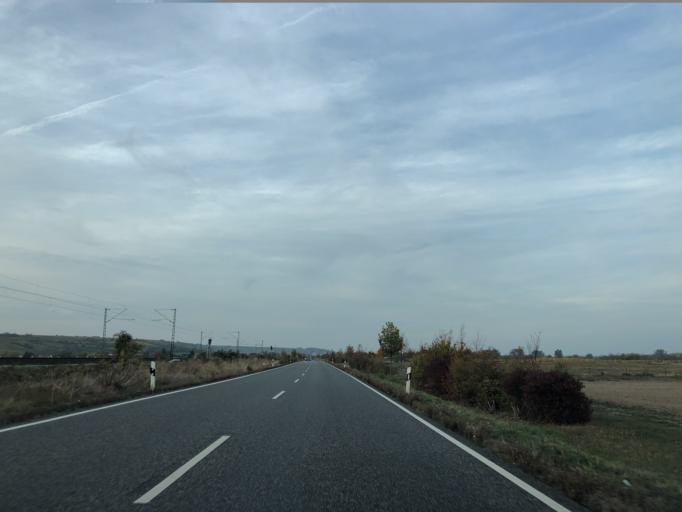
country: DE
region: Rheinland-Pfalz
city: Ludwigshohe
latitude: 49.8087
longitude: 8.3526
